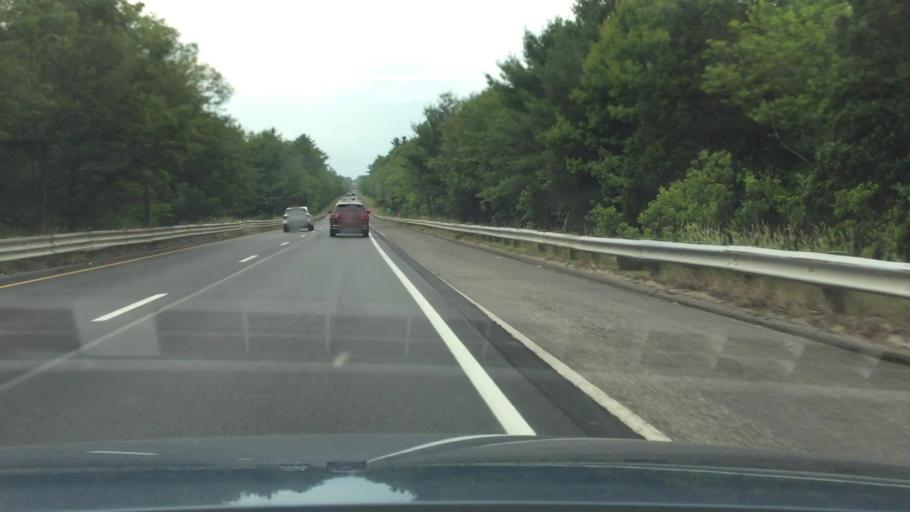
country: US
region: Massachusetts
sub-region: Plymouth County
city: Marshfield
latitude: 42.0690
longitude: -70.7302
